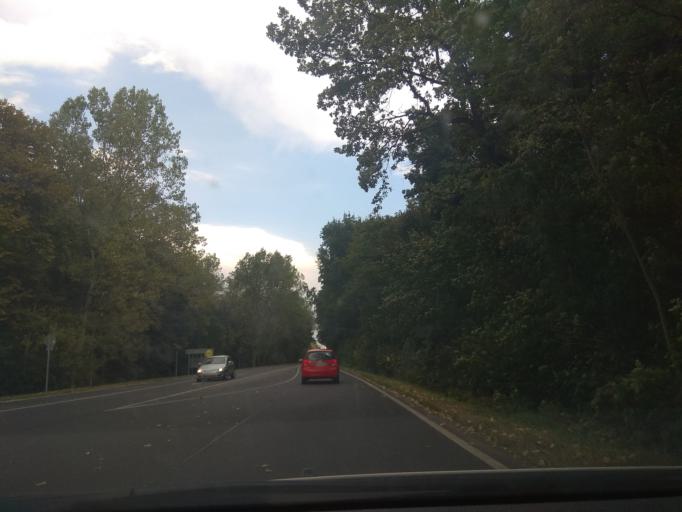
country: HU
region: Borsod-Abauj-Zemplen
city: Sajooeroes
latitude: 47.9300
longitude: 21.0254
